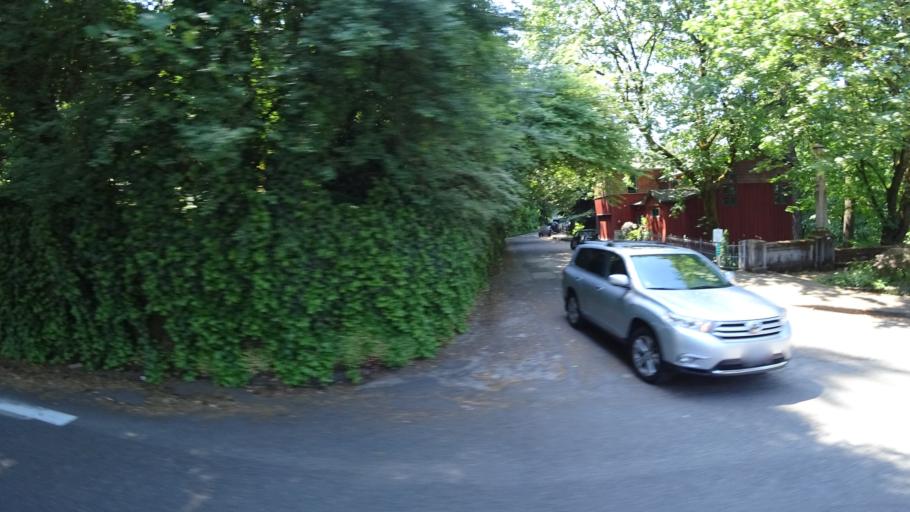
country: US
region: Oregon
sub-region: Multnomah County
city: Portland
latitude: 45.5184
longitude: -122.6973
